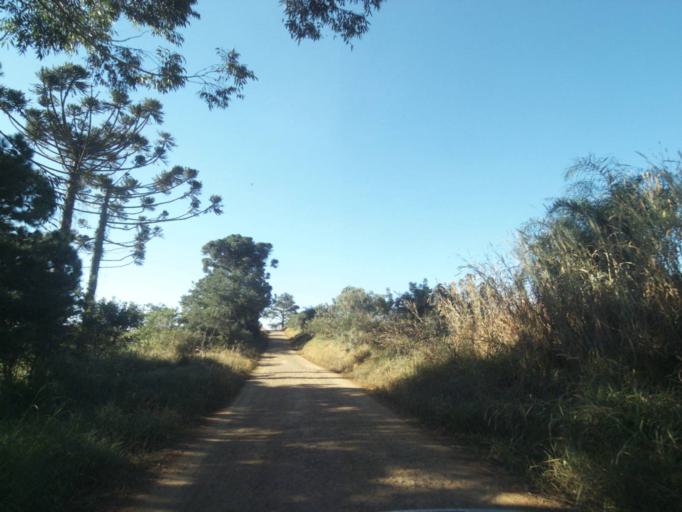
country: BR
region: Parana
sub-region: Tibagi
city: Tibagi
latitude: -24.5440
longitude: -50.5080
